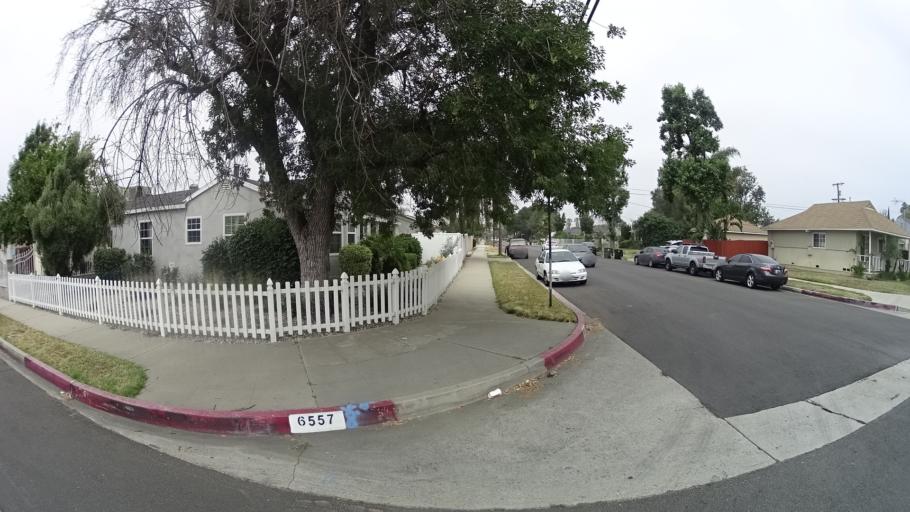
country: US
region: California
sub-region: Los Angeles County
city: North Hollywood
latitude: 34.1902
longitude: -118.4063
